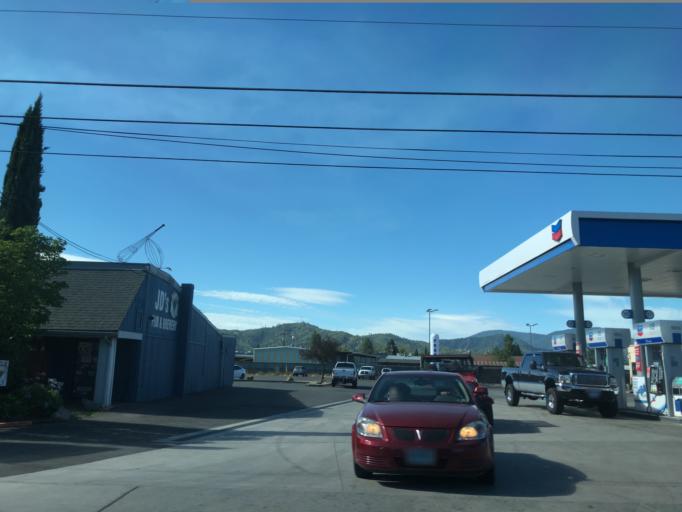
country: US
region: Oregon
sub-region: Josephine County
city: Grants Pass
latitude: 42.4236
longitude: -123.3404
